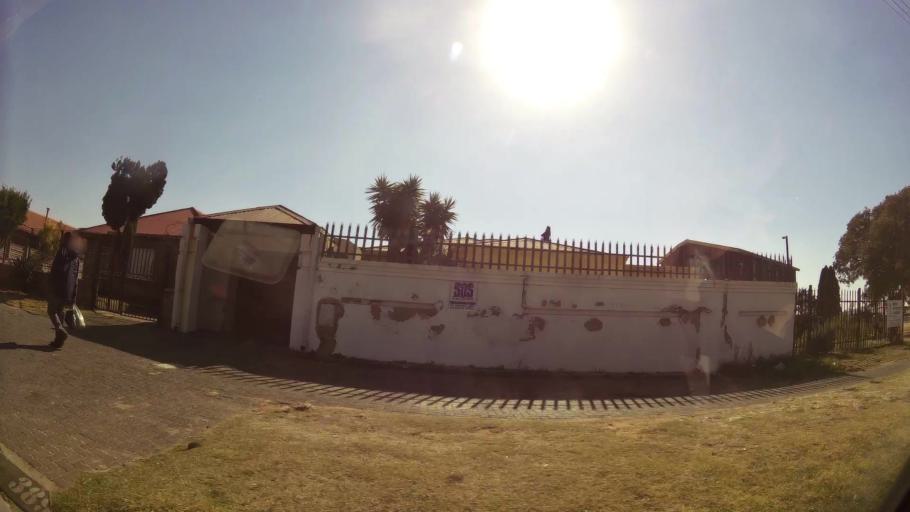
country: ZA
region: Gauteng
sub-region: City of Johannesburg Metropolitan Municipality
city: Johannesburg
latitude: -26.2561
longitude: 28.0478
